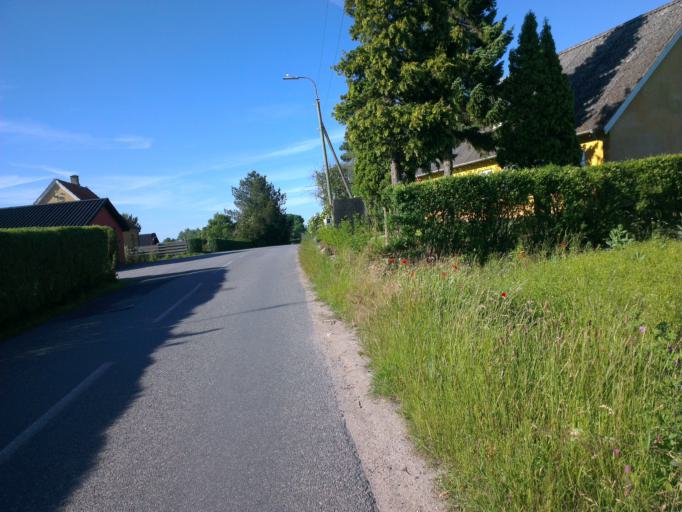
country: DK
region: Capital Region
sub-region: Frederikssund Kommune
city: Skibby
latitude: 55.7377
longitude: 12.0302
